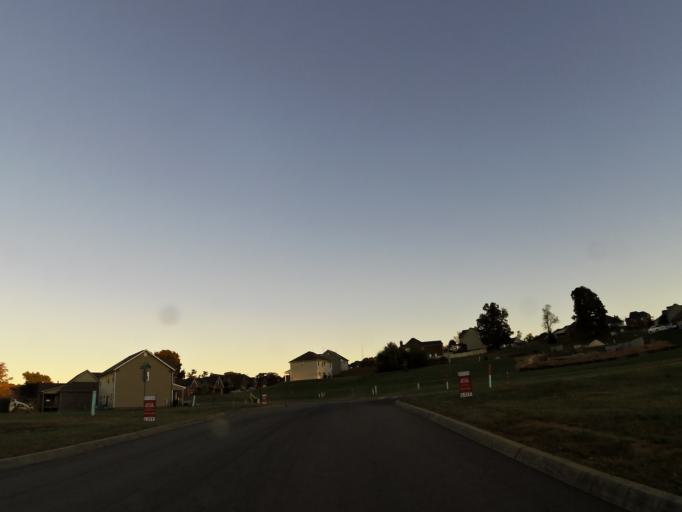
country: US
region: Tennessee
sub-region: Knox County
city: Knoxville
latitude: 36.0289
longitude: -83.9782
